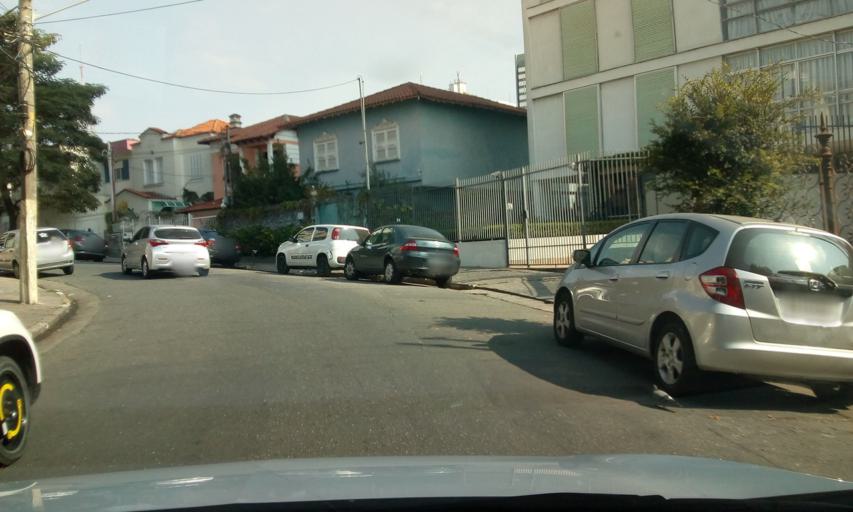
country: BR
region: Sao Paulo
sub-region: Sao Paulo
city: Sao Paulo
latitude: -23.5585
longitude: -46.6476
